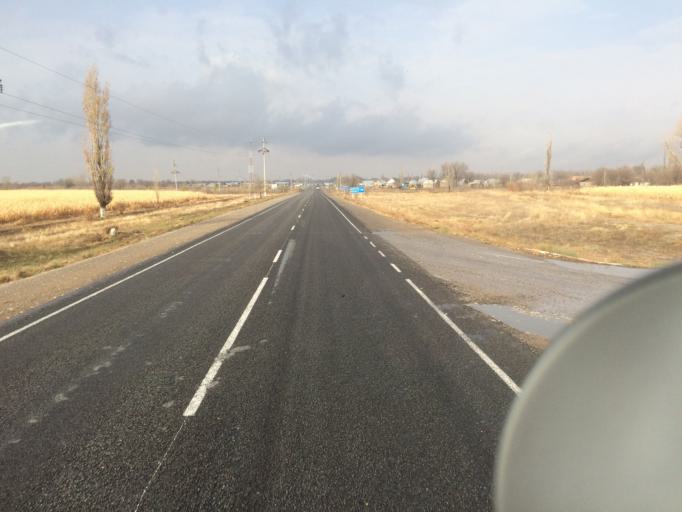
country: KZ
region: Zhambyl
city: Georgiyevka
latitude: 43.1558
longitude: 74.6002
